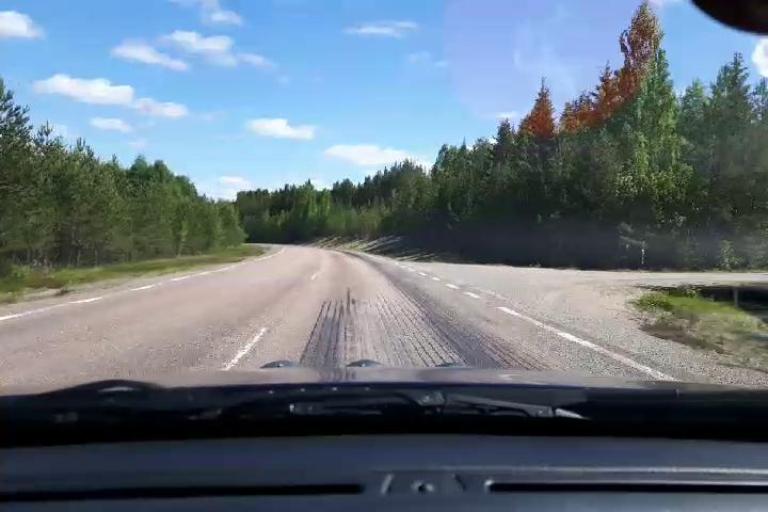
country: SE
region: Gaevleborg
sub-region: Ljusdals Kommun
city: Farila
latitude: 61.9362
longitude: 15.4017
